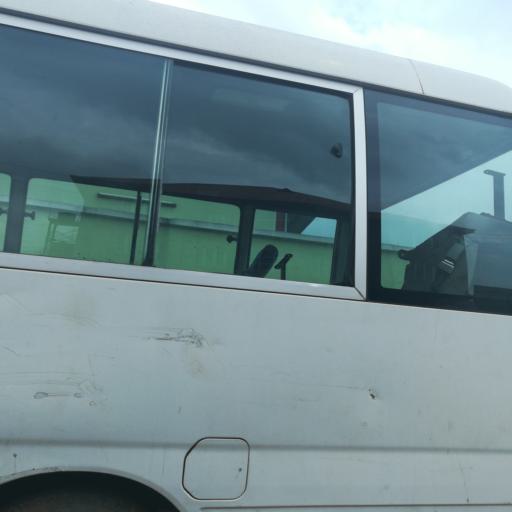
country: NG
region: Lagos
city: Ojota
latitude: 6.5860
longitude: 3.3872
